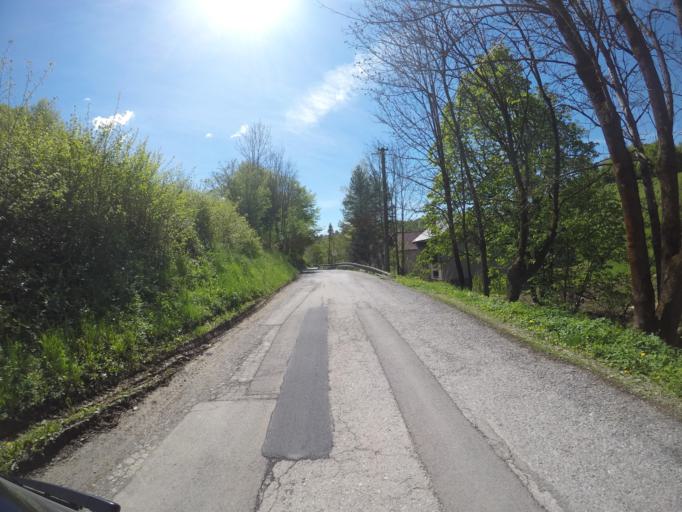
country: SK
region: Banskobystricky
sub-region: Okres Banska Bystrica
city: Banska Bystrica
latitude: 48.7124
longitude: 19.2296
